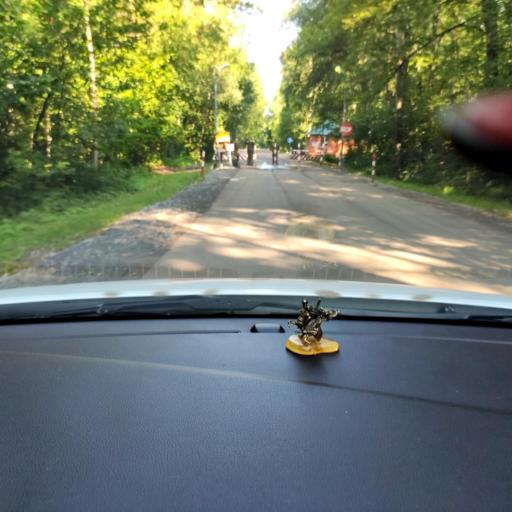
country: RU
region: Tatarstan
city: Stolbishchi
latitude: 55.7015
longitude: 49.2178
